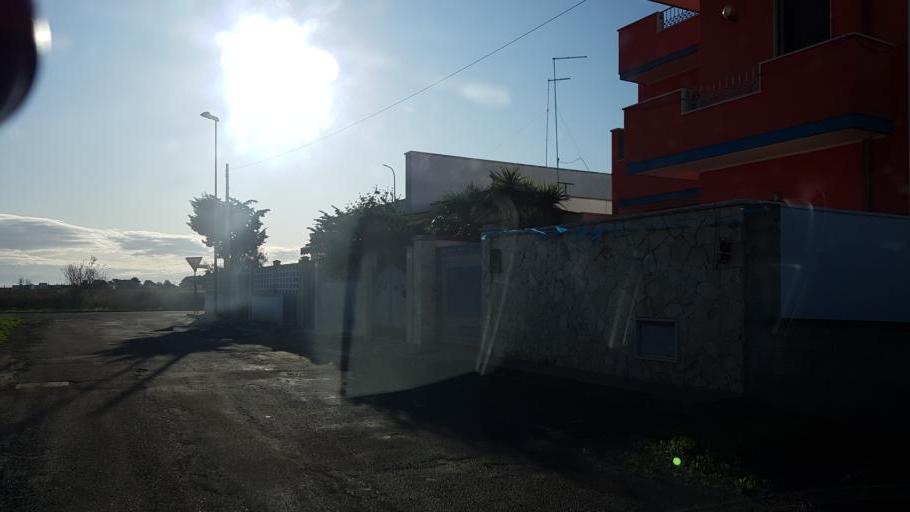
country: IT
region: Apulia
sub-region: Provincia di Brindisi
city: Torchiarolo
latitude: 40.5342
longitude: 18.0718
